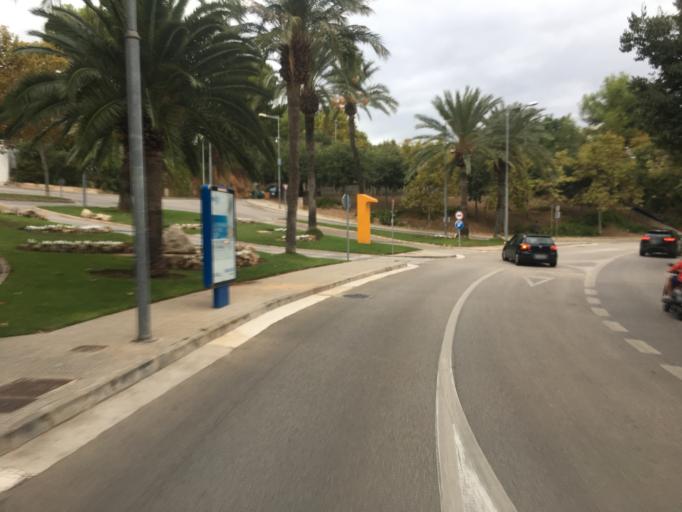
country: ES
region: Balearic Islands
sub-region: Illes Balears
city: Palma
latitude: 39.5466
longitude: 2.5950
